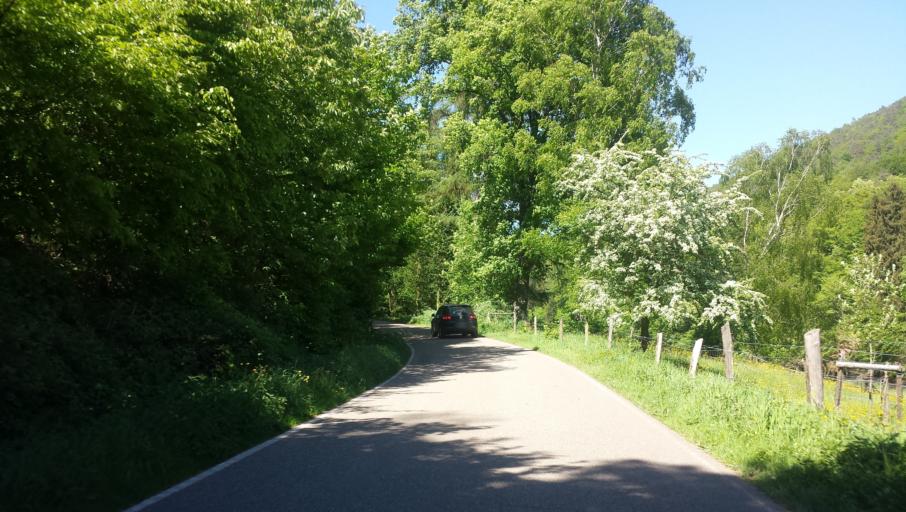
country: DE
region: Rheinland-Pfalz
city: Ramberg
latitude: 49.2729
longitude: 8.0299
